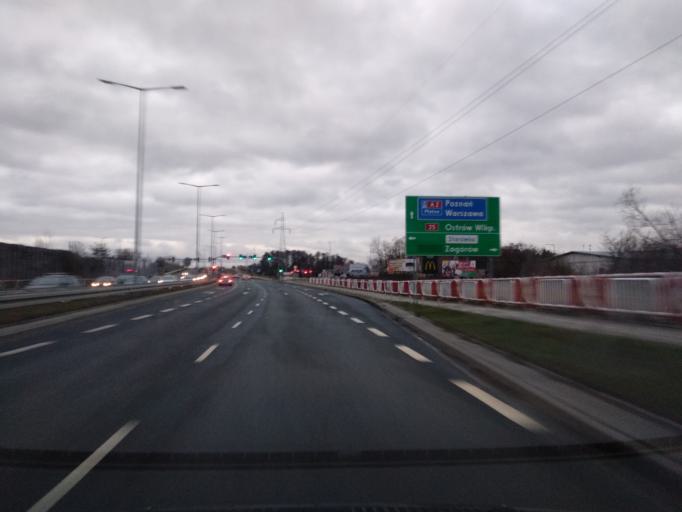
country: PL
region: Greater Poland Voivodeship
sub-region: Powiat koninski
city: Stare Miasto
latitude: 52.2044
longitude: 18.2256
